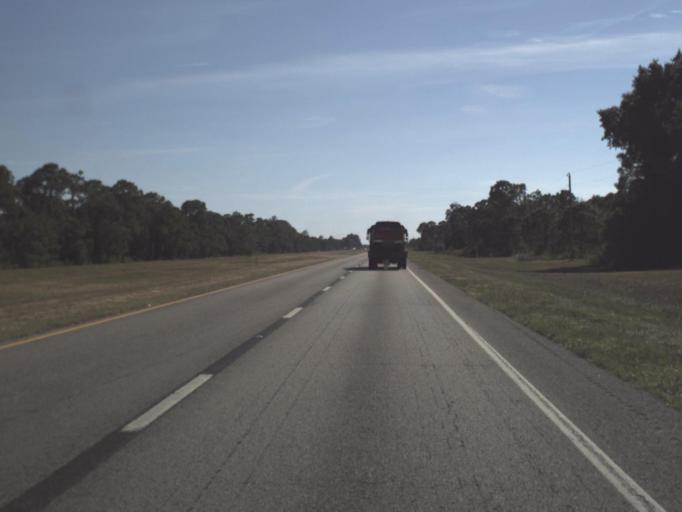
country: US
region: Florida
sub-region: Highlands County
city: Placid Lakes
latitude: 27.1044
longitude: -81.3326
